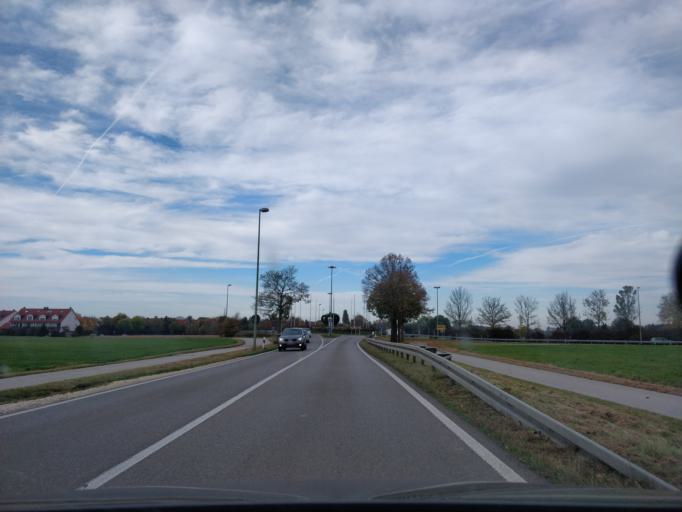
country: DE
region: Bavaria
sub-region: Swabia
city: Konigsbrunn
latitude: 48.2640
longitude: 10.9044
